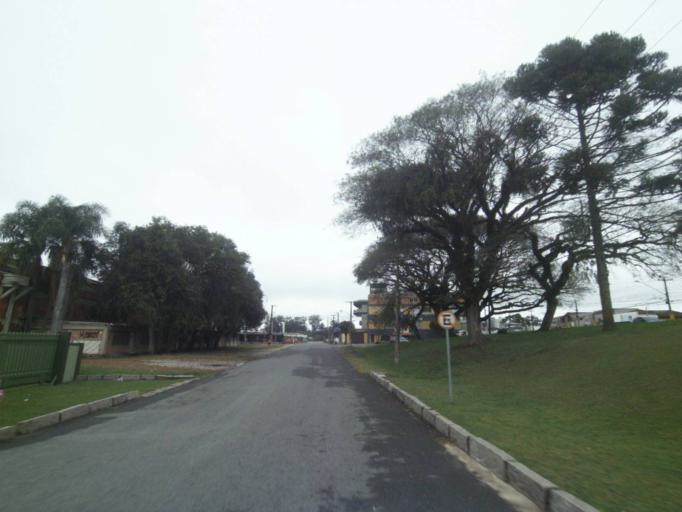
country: BR
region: Parana
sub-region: Curitiba
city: Curitiba
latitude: -25.5061
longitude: -49.2956
